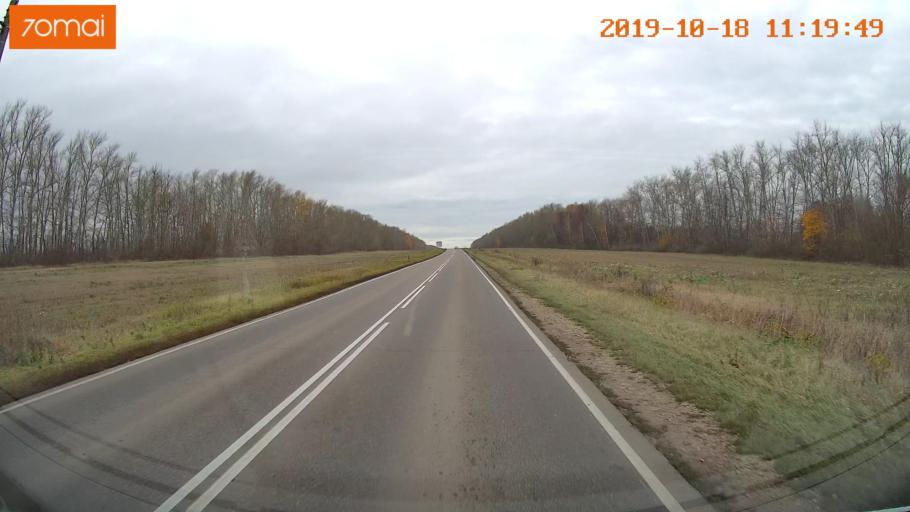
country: RU
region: Tula
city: Kimovsk
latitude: 54.0511
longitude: 38.5557
